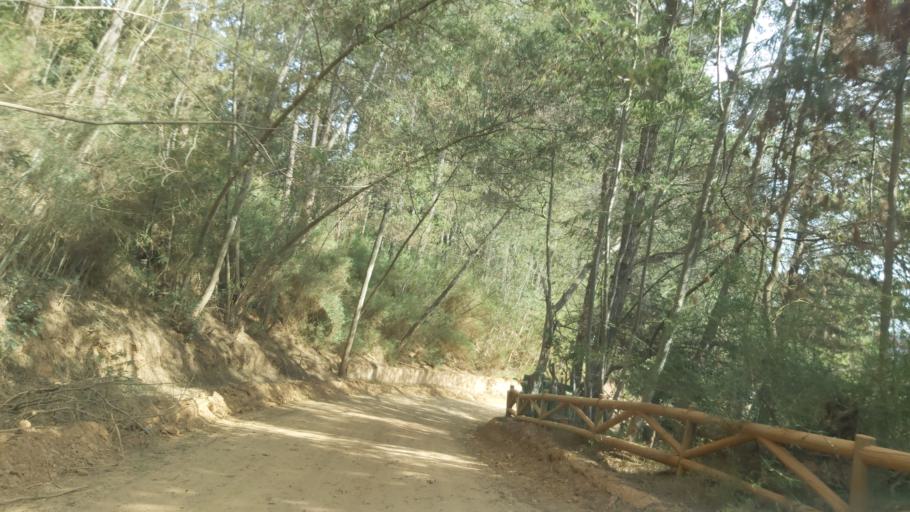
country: CL
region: Maule
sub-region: Provincia de Talca
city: Constitucion
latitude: -34.8427
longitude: -72.0401
